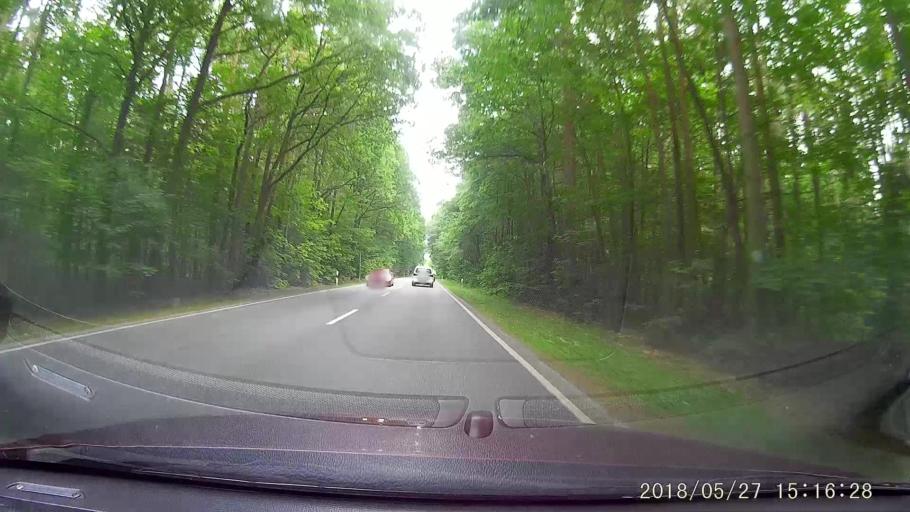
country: DE
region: Saxony
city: Niesky
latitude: 51.2773
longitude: 14.8242
